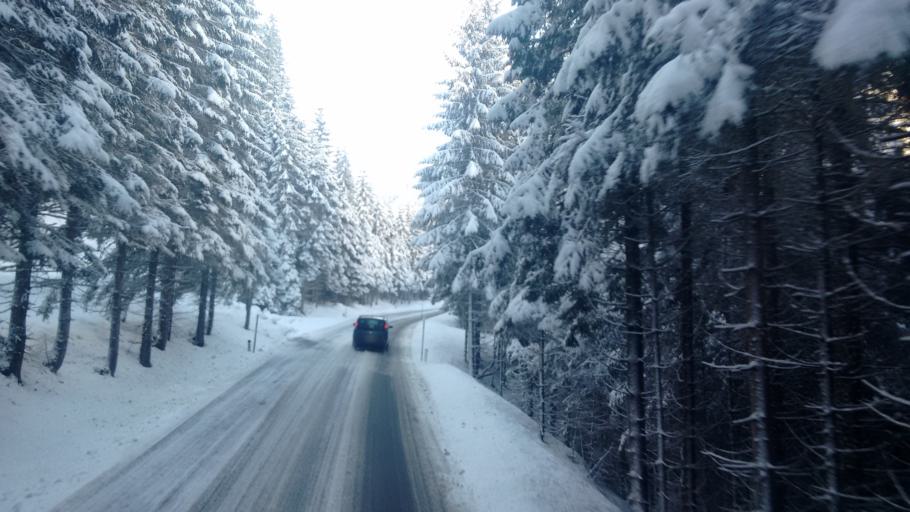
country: AT
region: Salzburg
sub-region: Politischer Bezirk Sankt Johann im Pongau
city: Flachau
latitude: 47.3261
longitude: 13.4453
